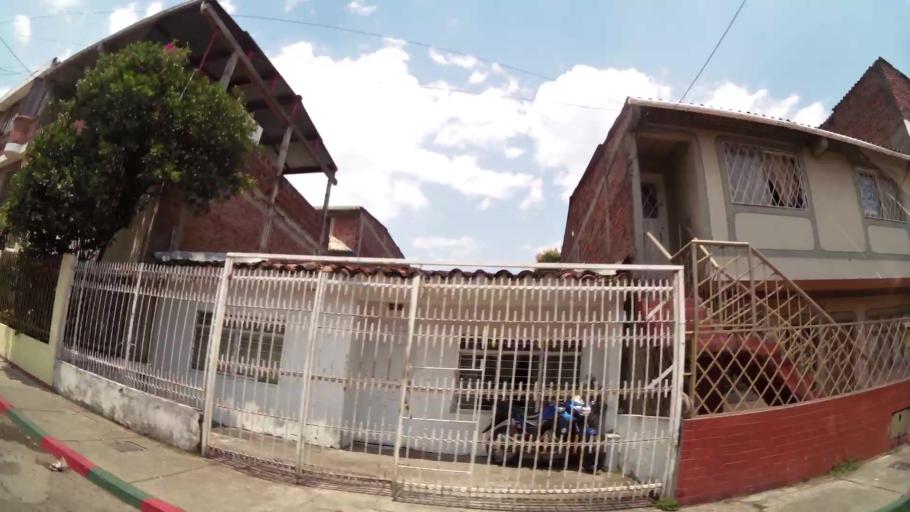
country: CO
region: Valle del Cauca
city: Cali
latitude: 3.4093
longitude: -76.5334
